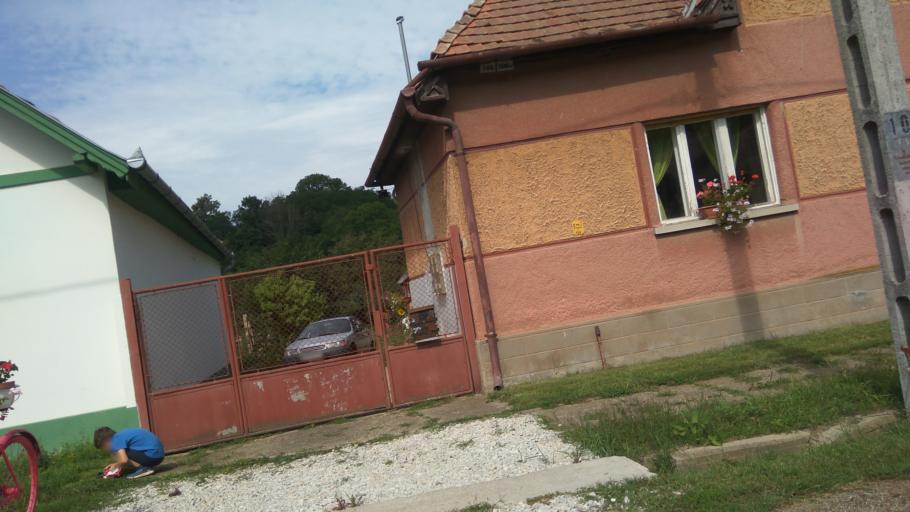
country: SK
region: Nitriansky
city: Sahy
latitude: 48.0317
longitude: 18.9135
